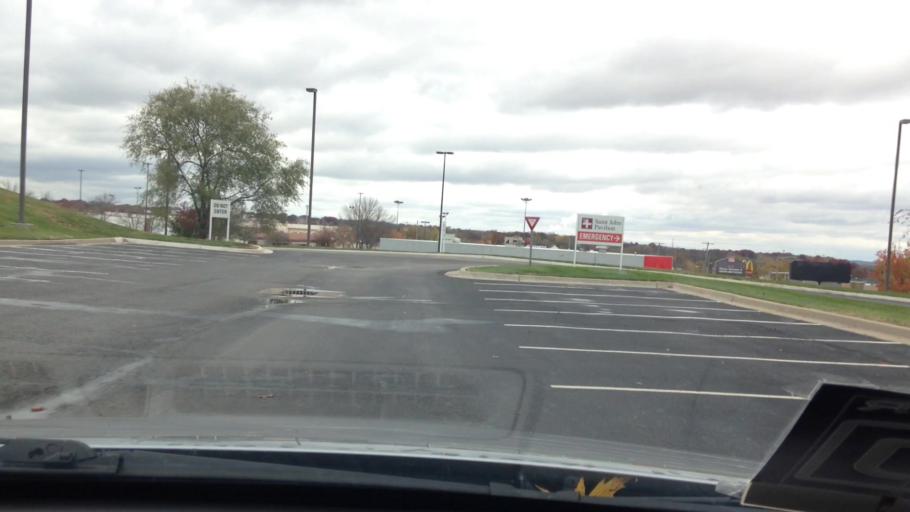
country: US
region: Kansas
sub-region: Leavenworth County
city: Leavenworth
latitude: 39.2832
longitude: -94.9041
